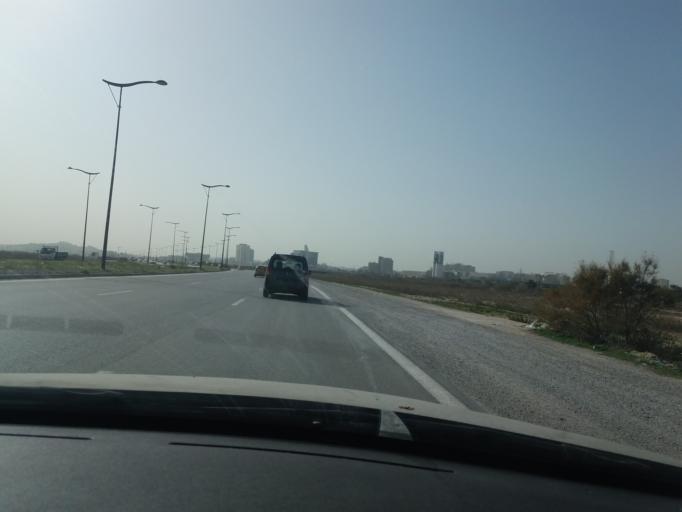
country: TN
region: Tunis
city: Tunis
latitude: 36.8176
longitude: 10.1965
